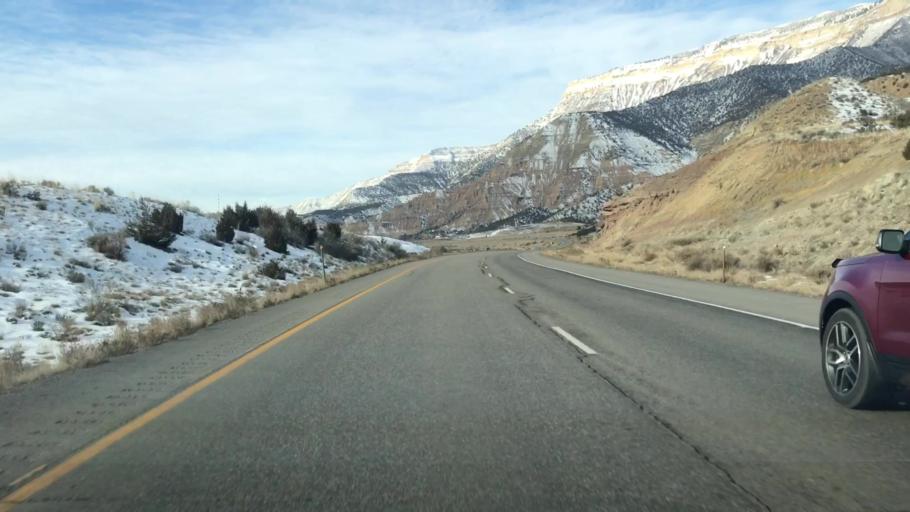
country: US
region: Colorado
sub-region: Garfield County
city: Battlement Mesa
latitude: 39.4992
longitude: -107.9204
